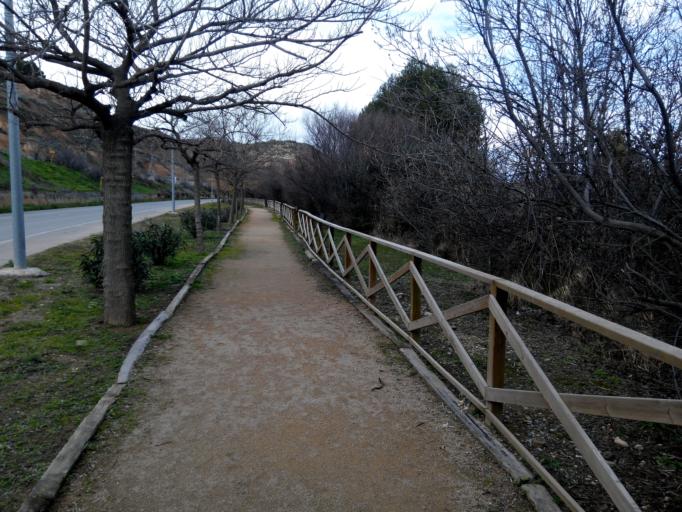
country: ES
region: Navarre
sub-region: Provincia de Navarra
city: Tudela
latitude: 42.0681
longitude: -1.6058
